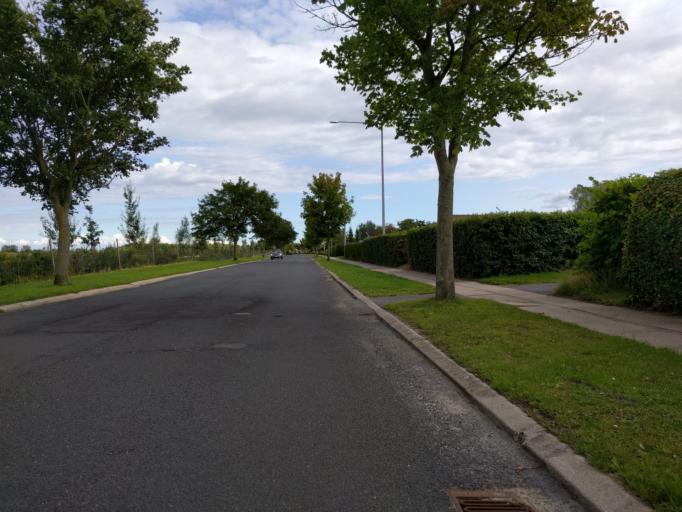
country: DK
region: South Denmark
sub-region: Kerteminde Kommune
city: Kerteminde
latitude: 55.4592
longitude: 10.6381
